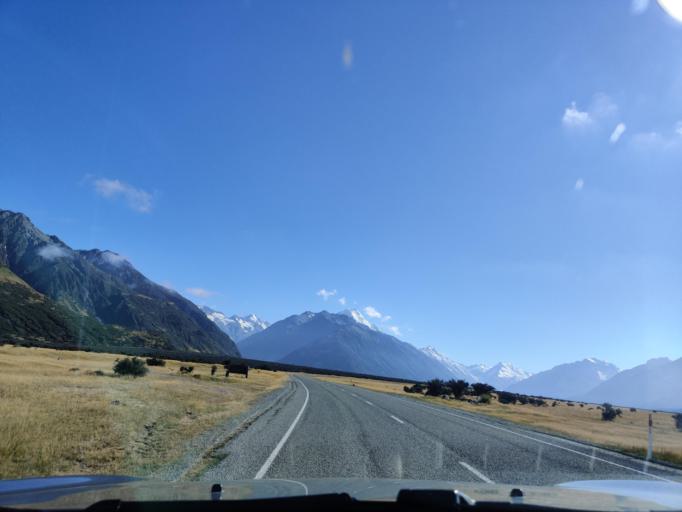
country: NZ
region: Canterbury
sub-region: Timaru District
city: Pleasant Point
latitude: -43.7899
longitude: 170.1196
